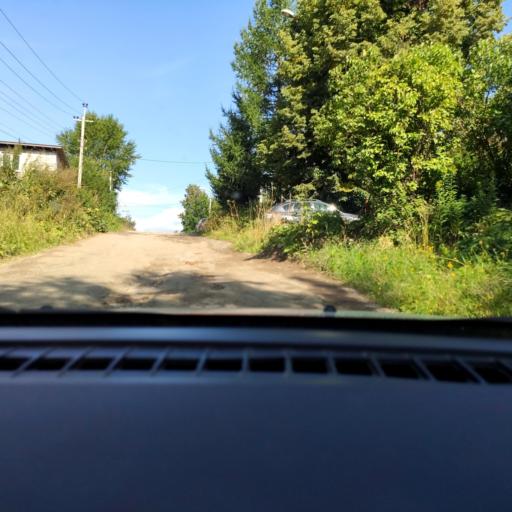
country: RU
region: Perm
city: Perm
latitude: 58.1157
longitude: 56.3931
